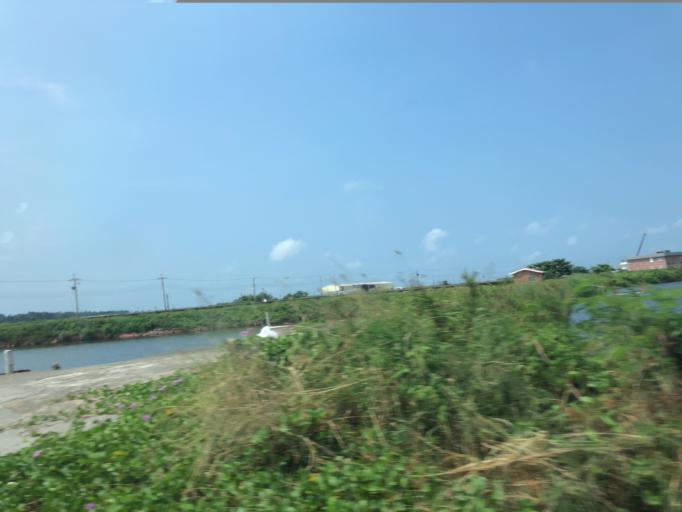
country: TW
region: Taiwan
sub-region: Chiayi
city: Taibao
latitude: 23.4645
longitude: 120.1512
